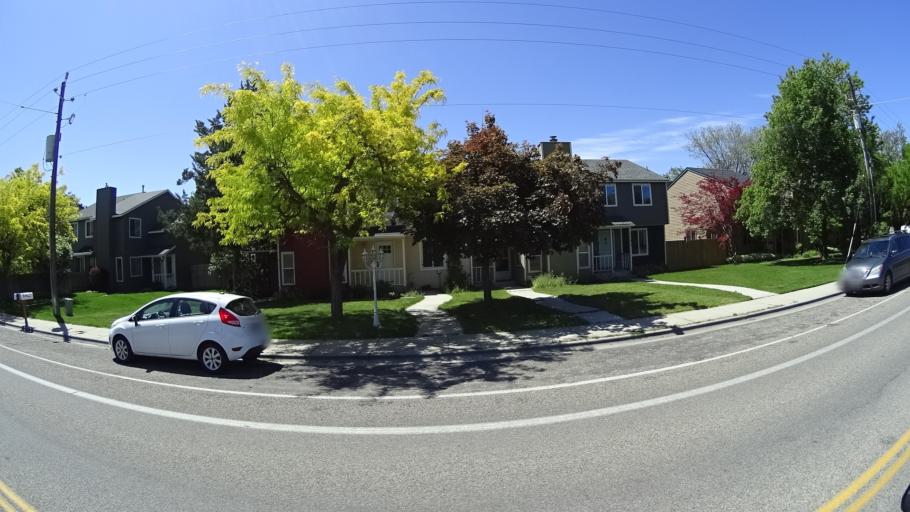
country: US
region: Idaho
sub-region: Ada County
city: Boise
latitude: 43.5741
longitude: -116.1612
